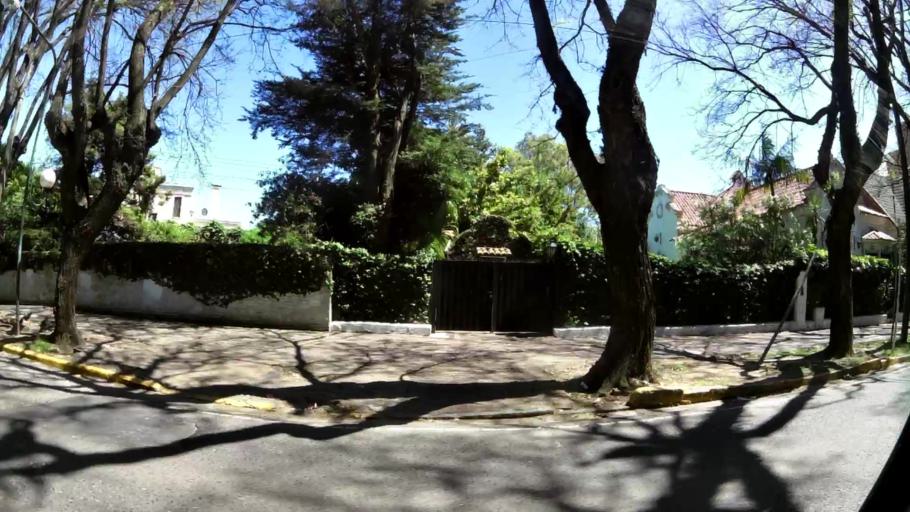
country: AR
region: Buenos Aires
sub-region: Partido de Vicente Lopez
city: Olivos
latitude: -34.5116
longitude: -58.4862
